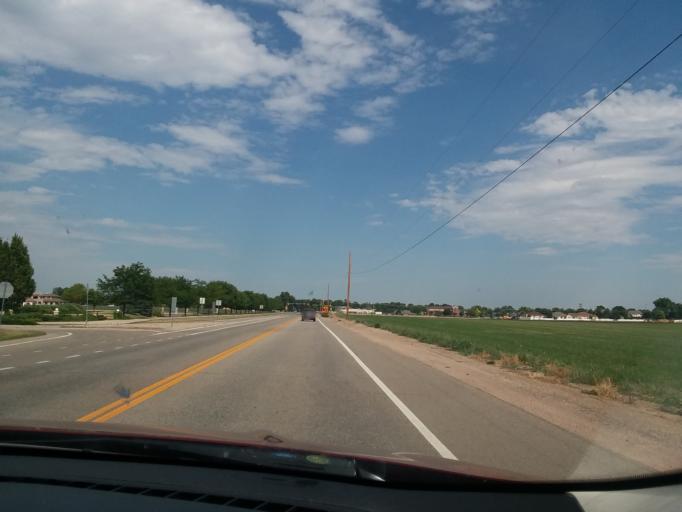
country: US
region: Colorado
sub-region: Larimer County
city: Berthoud
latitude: 40.3051
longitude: -105.0986
